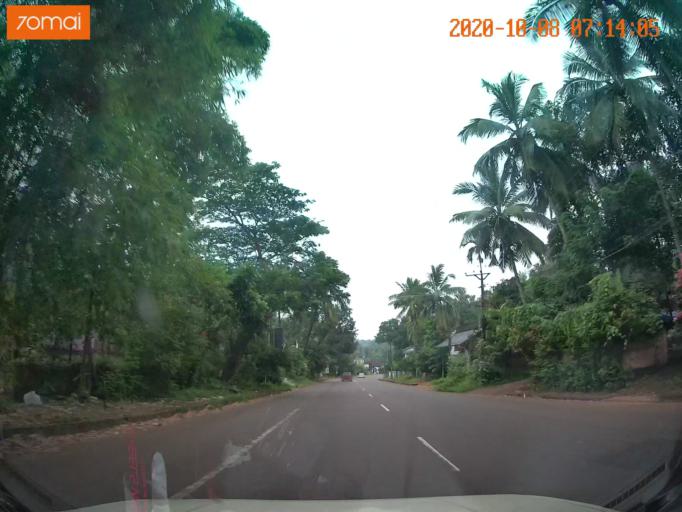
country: IN
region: Kerala
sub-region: Malappuram
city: Ponnani
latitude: 10.8154
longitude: 76.0151
